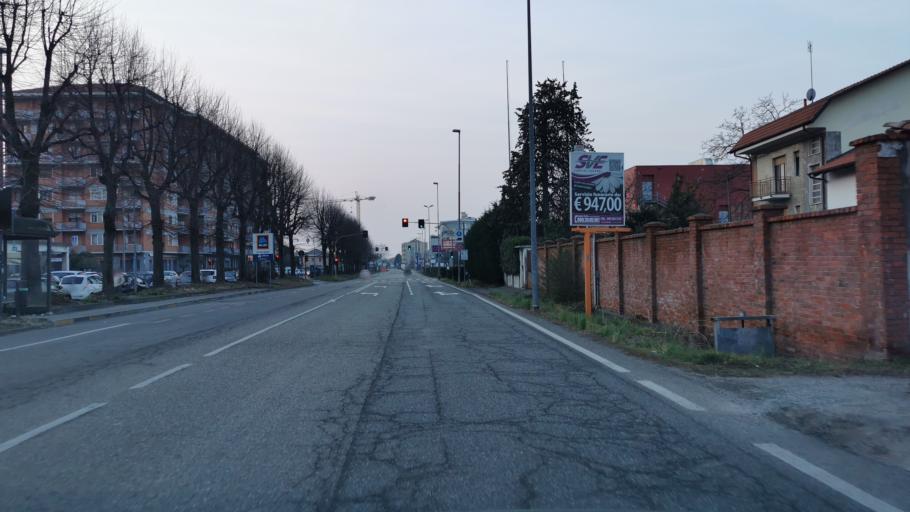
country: IT
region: Piedmont
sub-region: Provincia di Torino
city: Borgaro Torinese
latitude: 45.1563
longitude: 7.6548
